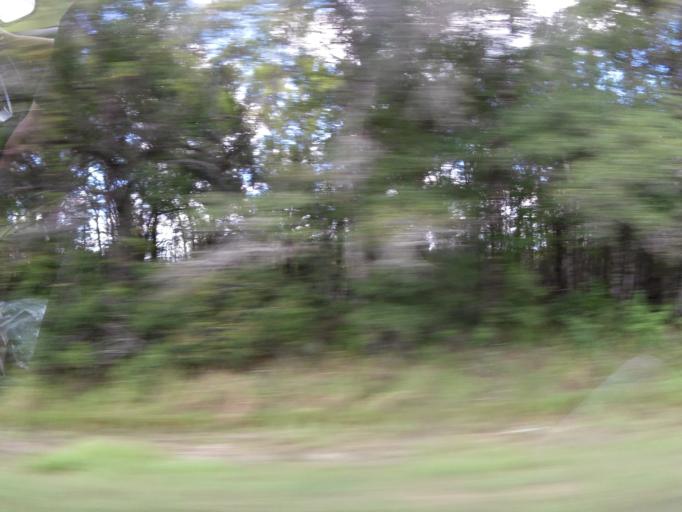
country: US
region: Florida
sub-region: Hamilton County
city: Jasper
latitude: 30.6772
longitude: -82.7029
